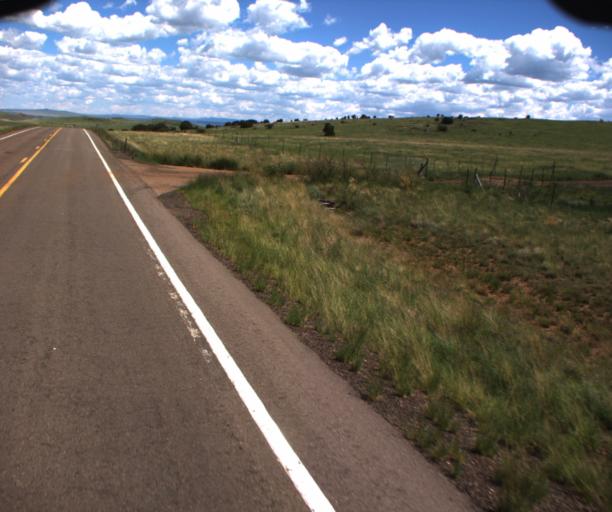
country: US
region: Arizona
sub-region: Apache County
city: Springerville
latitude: 34.2185
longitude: -109.4728
